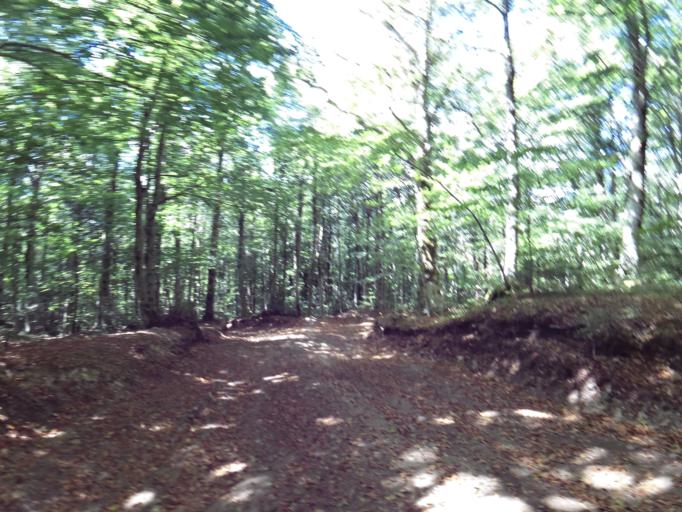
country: IT
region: Calabria
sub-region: Provincia di Vibo-Valentia
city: Mongiana
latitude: 38.5231
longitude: 16.3456
